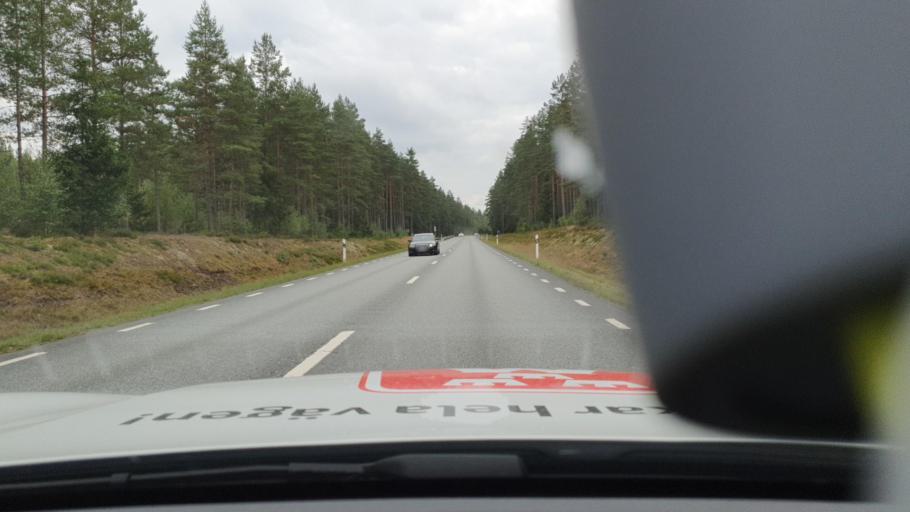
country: SE
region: Joenkoeping
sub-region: Gislaveds Kommun
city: Gislaved
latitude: 57.4095
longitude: 13.5997
